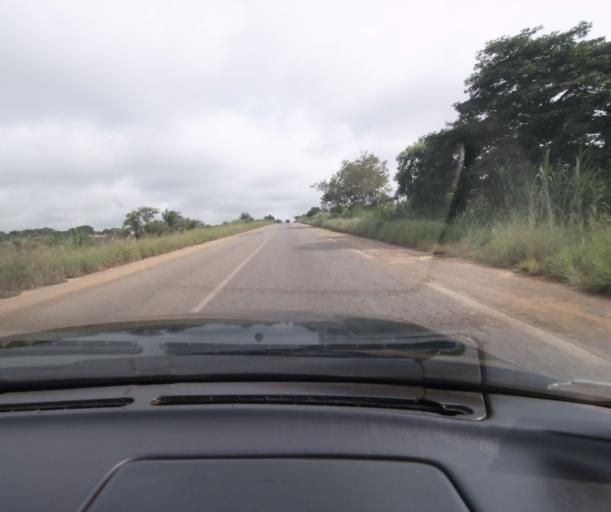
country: CM
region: Centre
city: Ombesa
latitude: 4.4006
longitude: 11.2498
